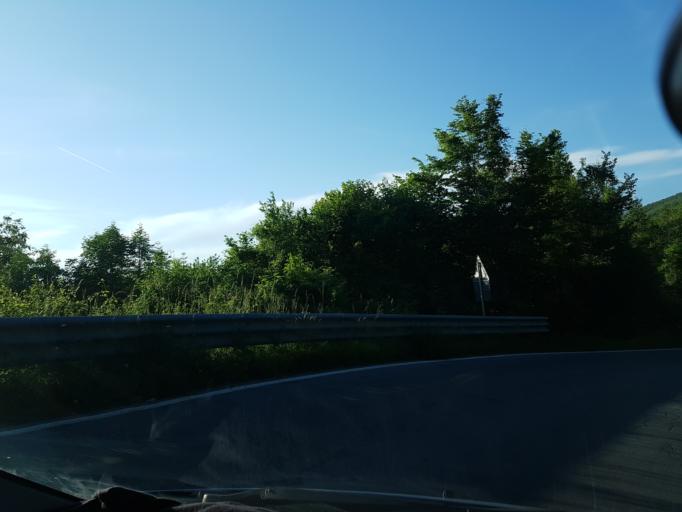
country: IT
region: Tuscany
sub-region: Provincia di Lucca
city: Minucciano
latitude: 44.1656
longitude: 10.2100
